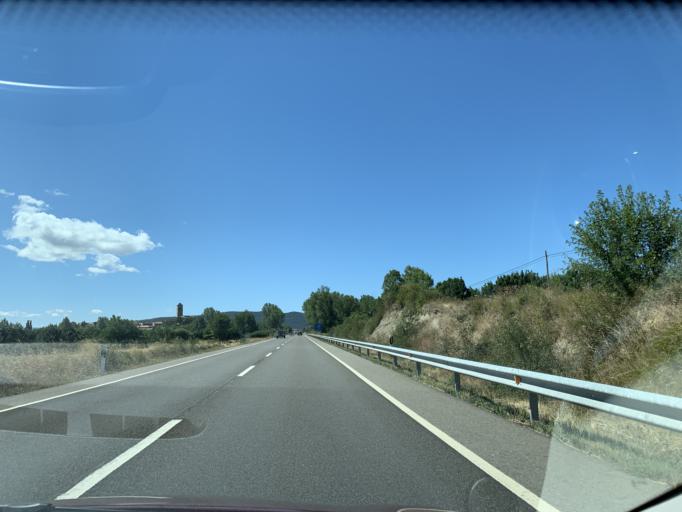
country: ES
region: Aragon
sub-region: Provincia de Huesca
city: Sabinanigo
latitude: 42.5540
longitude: -0.3407
